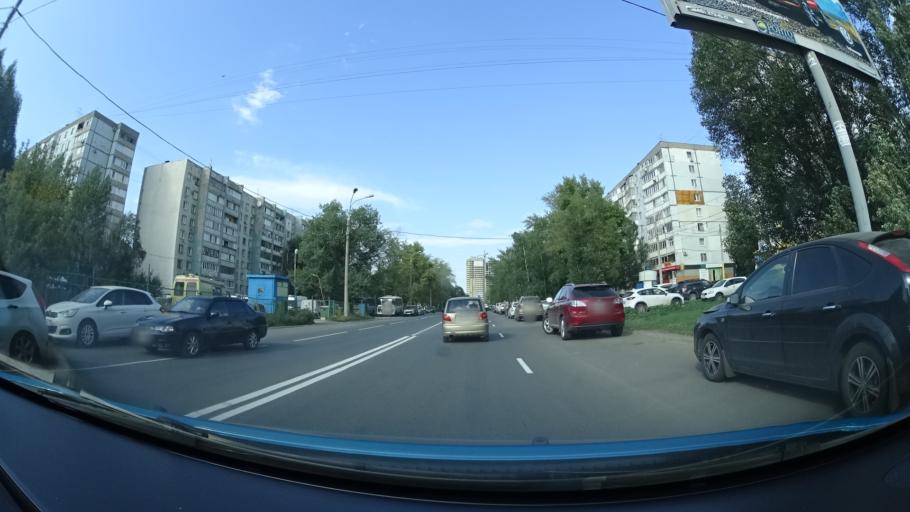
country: RU
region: Samara
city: Samara
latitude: 53.2620
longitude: 50.2249
